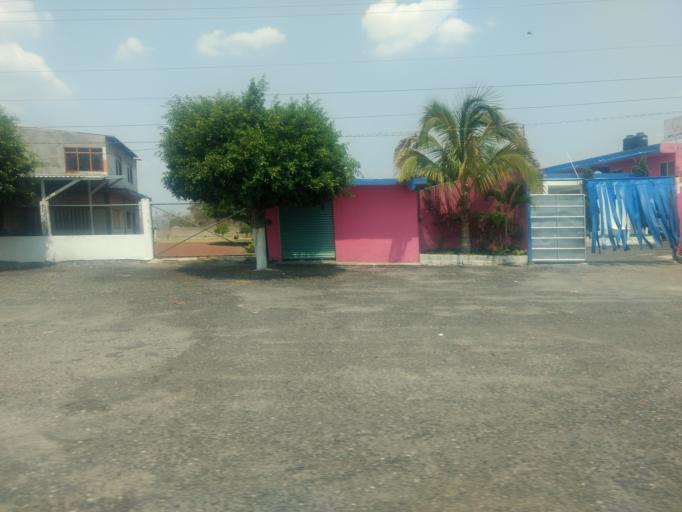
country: MX
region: Morelos
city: Xoxocotla
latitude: 18.7064
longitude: -99.2755
